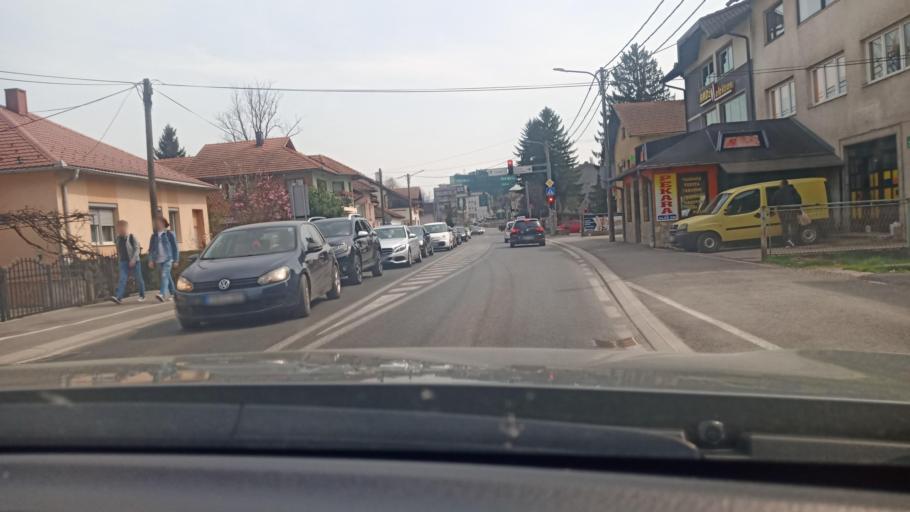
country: BA
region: Federation of Bosnia and Herzegovina
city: Bihac
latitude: 44.8182
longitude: 15.8652
